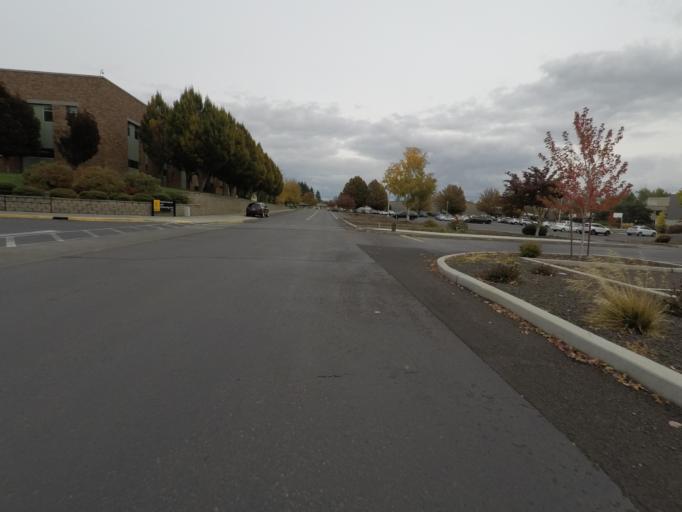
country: US
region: Washington
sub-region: Walla Walla County
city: Walla Walla East
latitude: 46.0801
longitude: -118.2779
